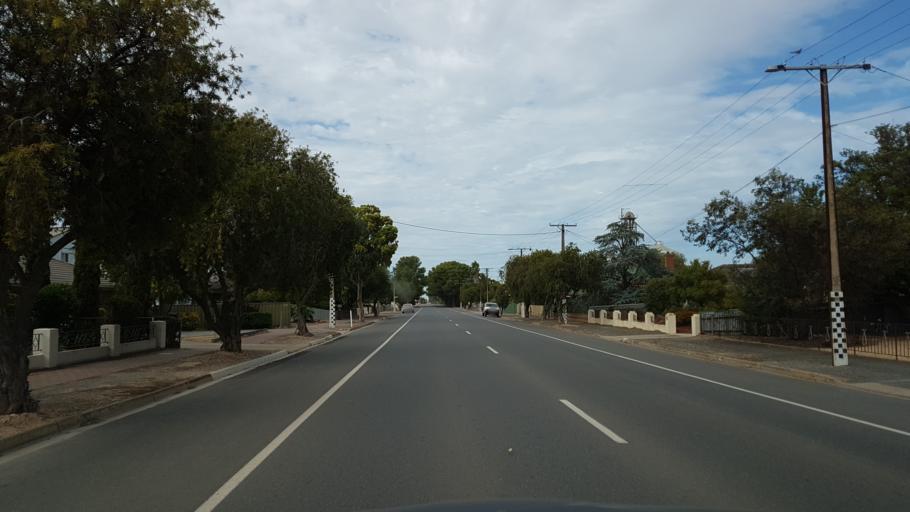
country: AU
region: South Australia
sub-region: Mallala
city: Mallala
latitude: -34.4398
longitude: 138.5099
